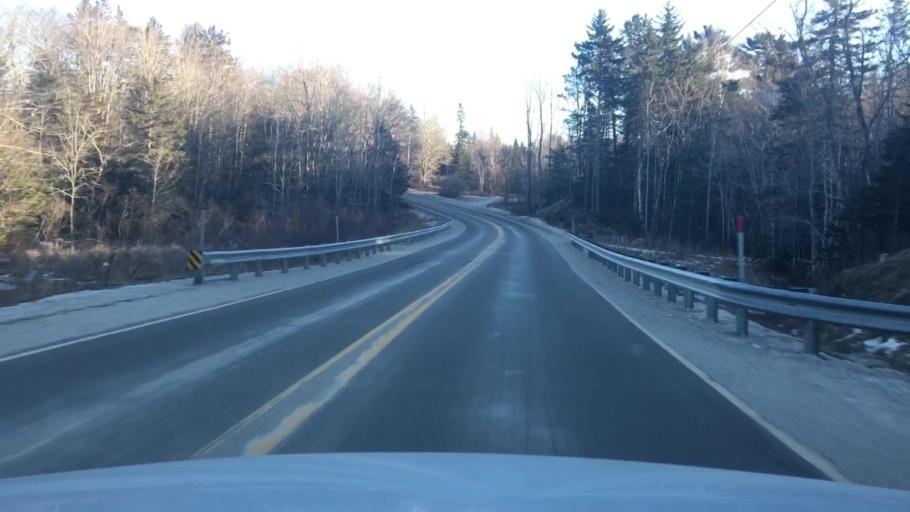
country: US
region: Maine
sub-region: Hancock County
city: Penobscot
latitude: 44.3876
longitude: -68.6972
